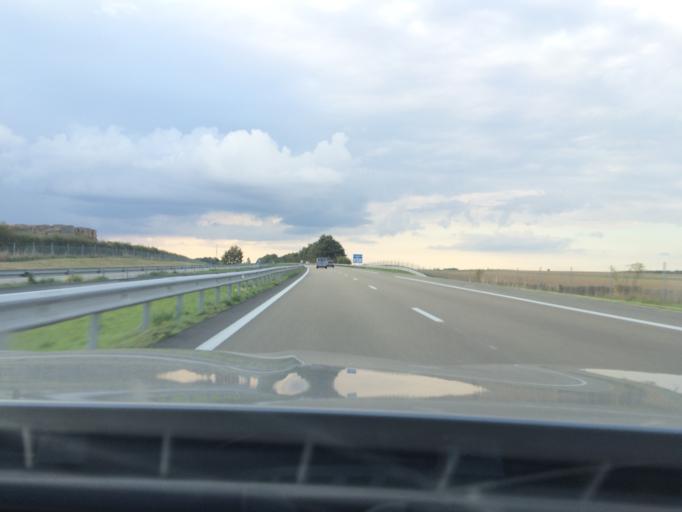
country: FR
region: Ile-de-France
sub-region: Departement de Seine-et-Marne
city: Egreville
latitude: 48.1529
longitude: 2.8976
